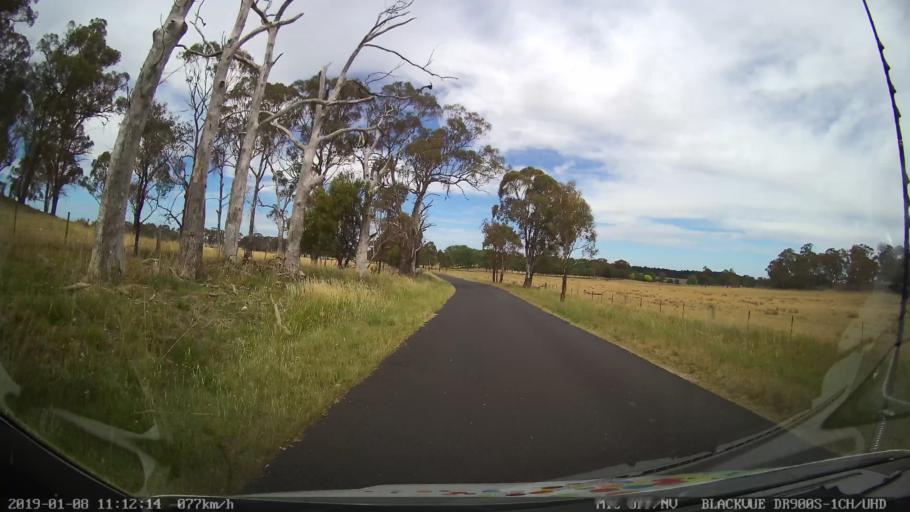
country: AU
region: New South Wales
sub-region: Guyra
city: Guyra
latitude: -30.2275
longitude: 151.6141
